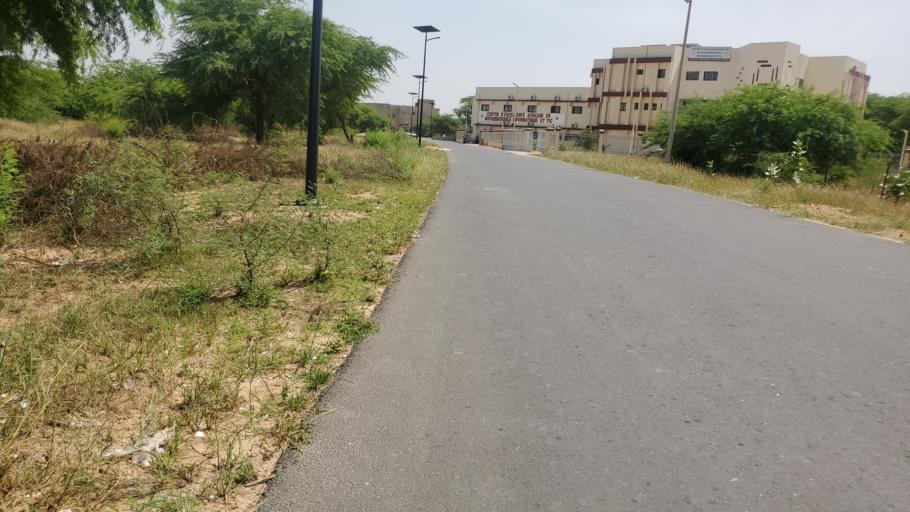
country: SN
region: Saint-Louis
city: Saint-Louis
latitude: 16.0570
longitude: -16.4270
